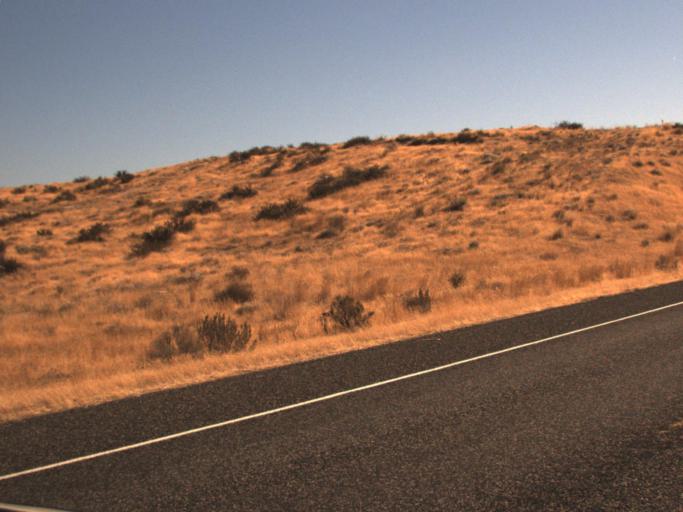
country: US
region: Washington
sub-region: Benton County
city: West Richland
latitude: 46.3378
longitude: -119.3395
